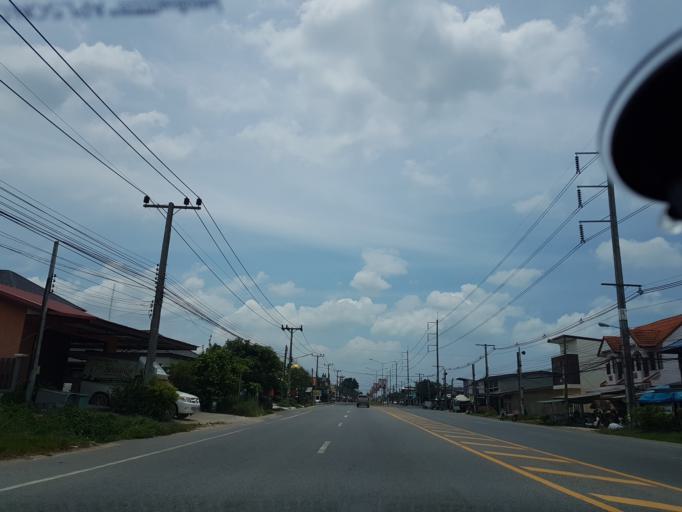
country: TH
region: Songkhla
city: Songkhla
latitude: 7.1022
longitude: 100.6333
